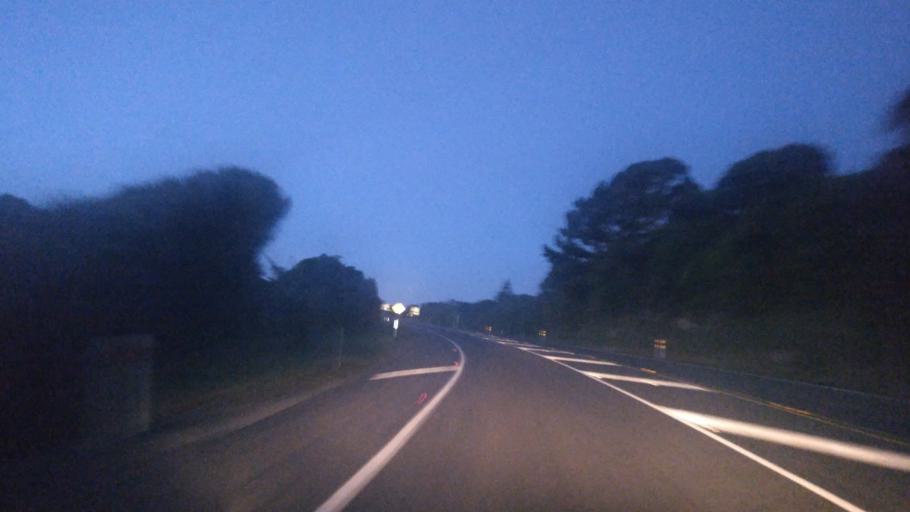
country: NZ
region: Wellington
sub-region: Porirua City
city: Porirua
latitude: -41.0440
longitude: 174.8838
